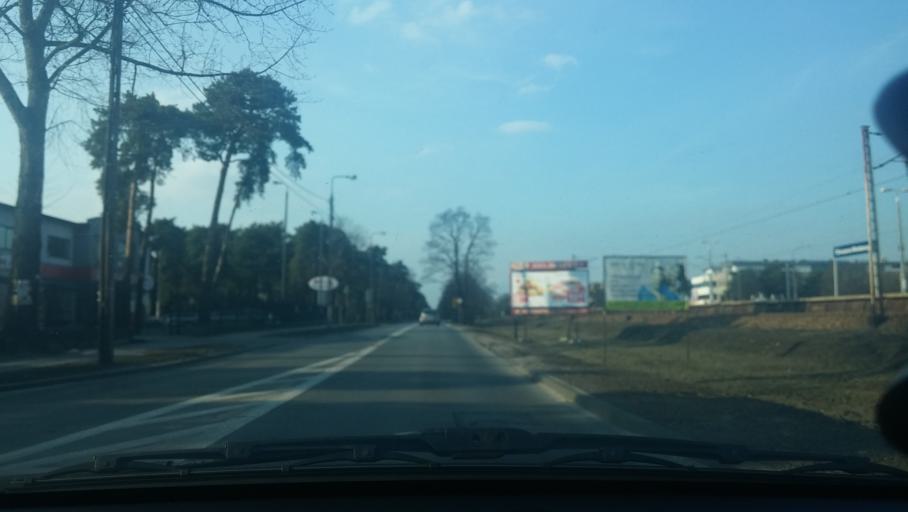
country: PL
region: Masovian Voivodeship
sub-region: Warszawa
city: Wawer
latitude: 52.1717
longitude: 21.2008
